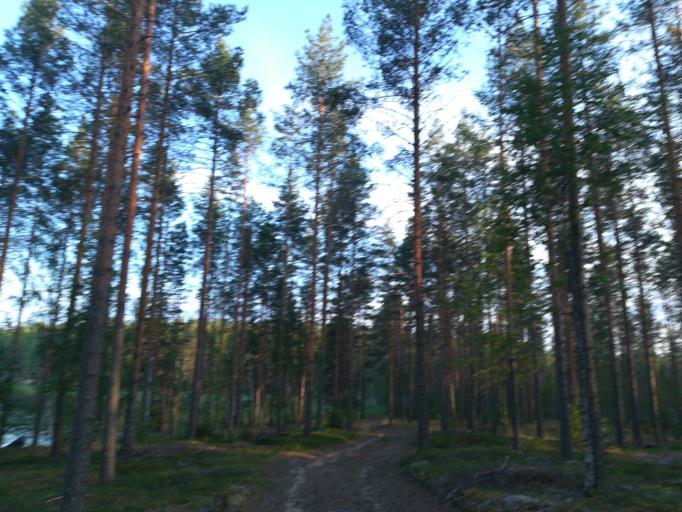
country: FI
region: Southern Savonia
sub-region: Mikkeli
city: Puumala
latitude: 61.4323
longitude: 28.4641
